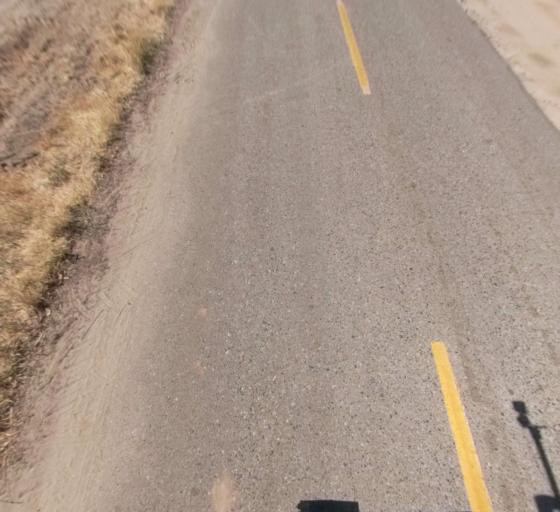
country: US
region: California
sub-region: Fresno County
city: Biola
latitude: 36.8576
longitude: -120.0283
